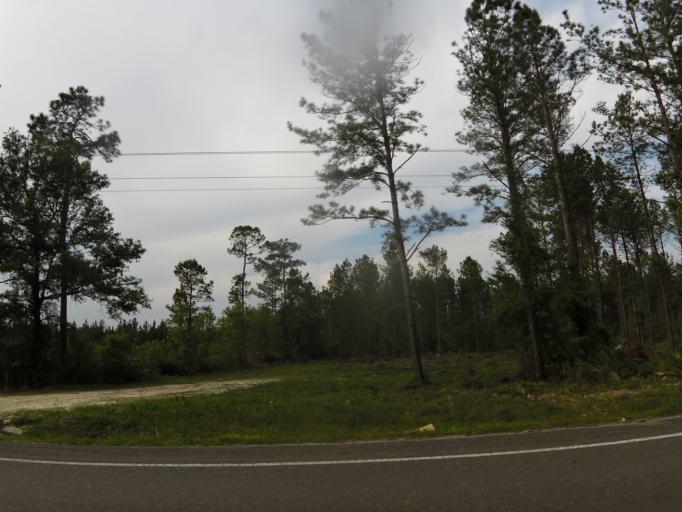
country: US
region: Georgia
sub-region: Camden County
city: Kingsland
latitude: 30.6995
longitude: -81.7646
